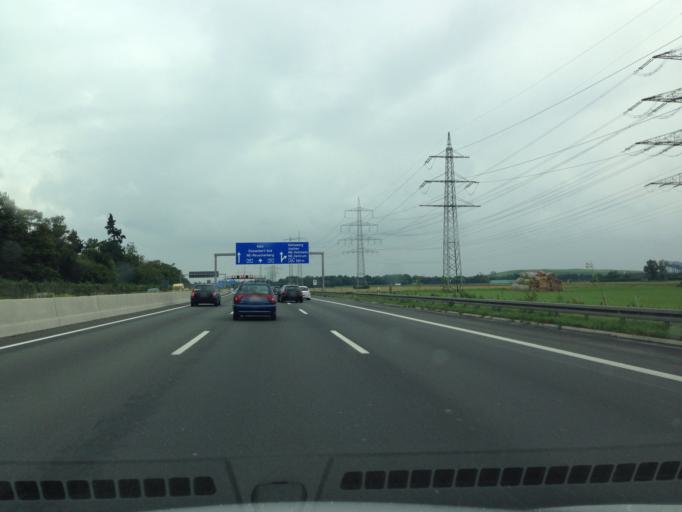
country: DE
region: North Rhine-Westphalia
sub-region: Regierungsbezirk Dusseldorf
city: Neuss
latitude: 51.1930
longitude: 6.6572
